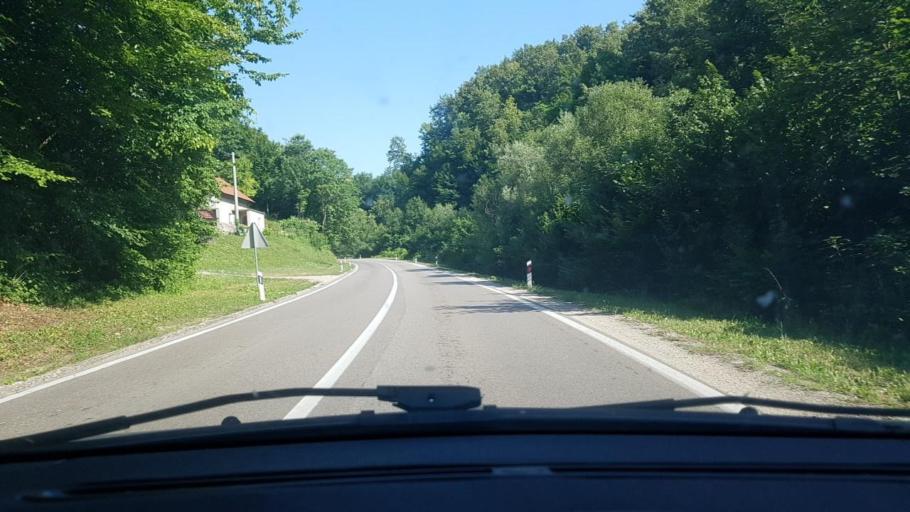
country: BA
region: Federation of Bosnia and Herzegovina
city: Skokovi
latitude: 45.0095
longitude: 15.9051
